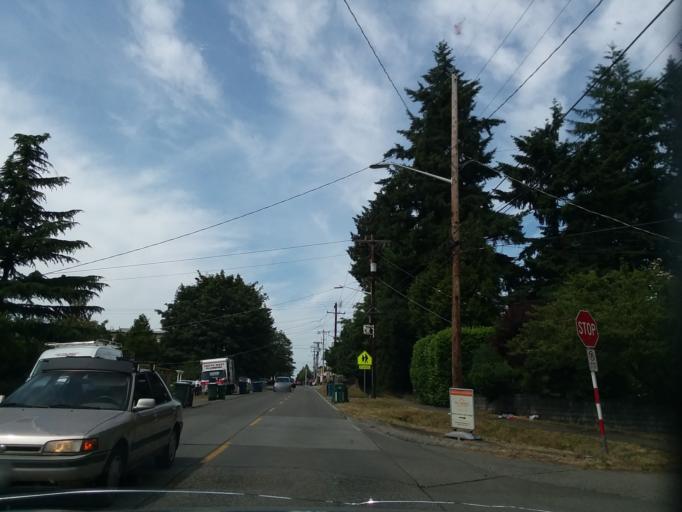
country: US
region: Washington
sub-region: King County
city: Shoreline
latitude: 47.7113
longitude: -122.3124
